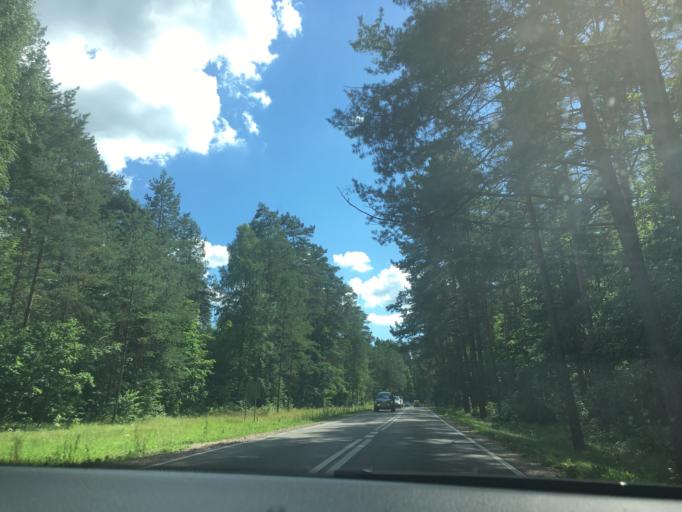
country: PL
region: Podlasie
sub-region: Powiat augustowski
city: Augustow
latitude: 53.8637
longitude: 23.0891
